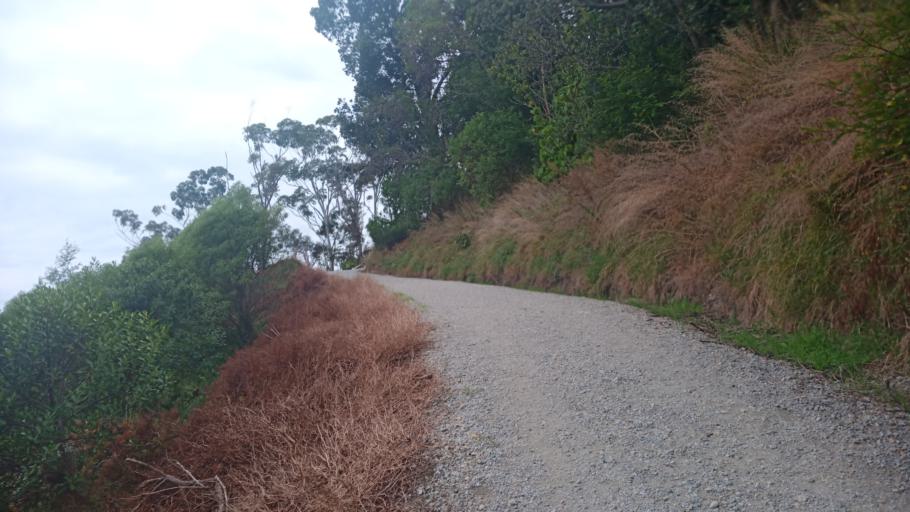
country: NZ
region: Gisborne
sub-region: Gisborne District
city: Gisborne
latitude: -38.6744
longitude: 178.0289
